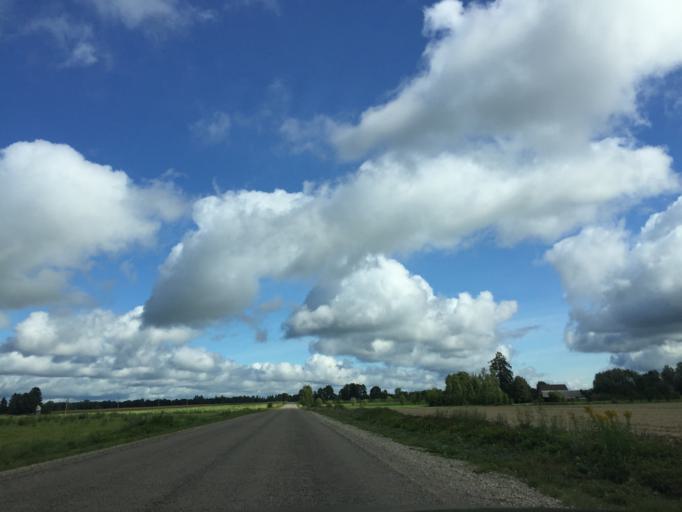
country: LV
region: Sigulda
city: Sigulda
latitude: 57.1876
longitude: 24.9395
